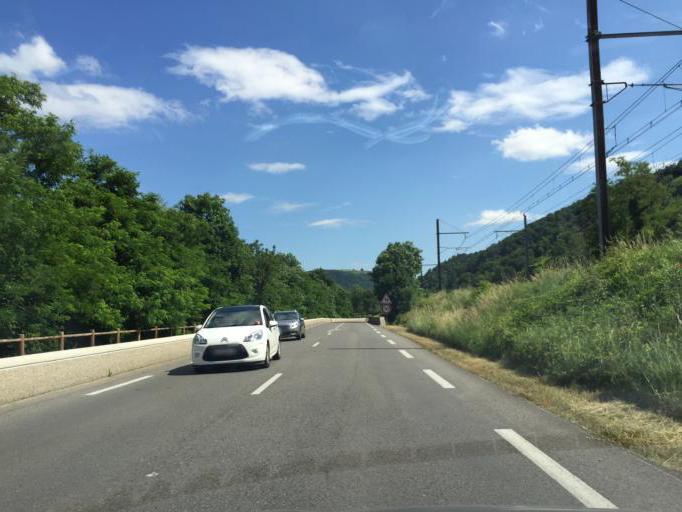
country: FR
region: Rhone-Alpes
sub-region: Departement de la Drome
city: Saint-Vallier
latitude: 45.1651
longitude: 4.8086
